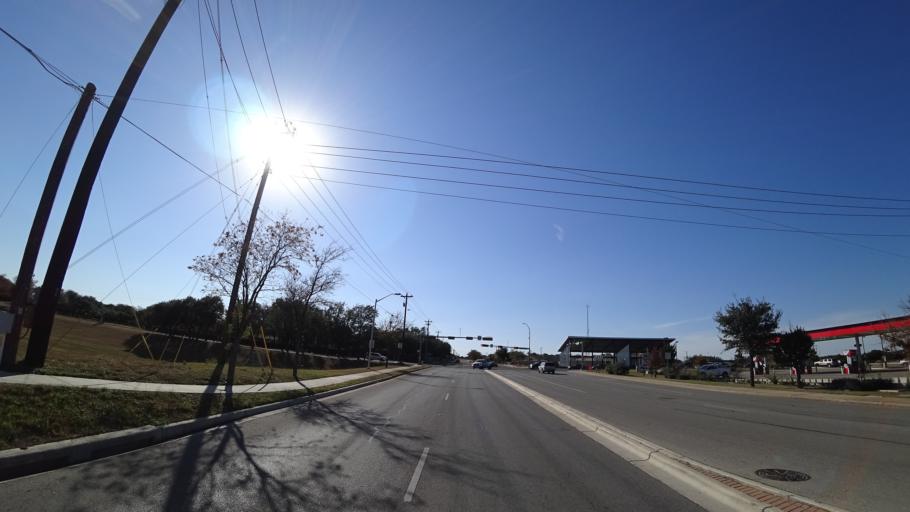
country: US
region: Texas
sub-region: Williamson County
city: Cedar Park
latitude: 30.5274
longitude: -97.8545
